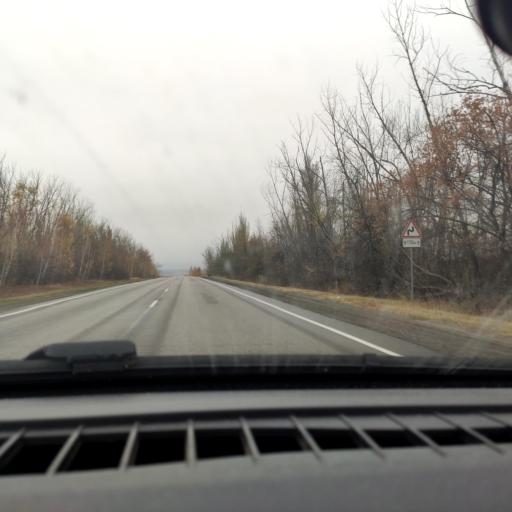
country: RU
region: Voronezj
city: Ostrogozhsk
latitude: 51.0162
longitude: 38.9859
